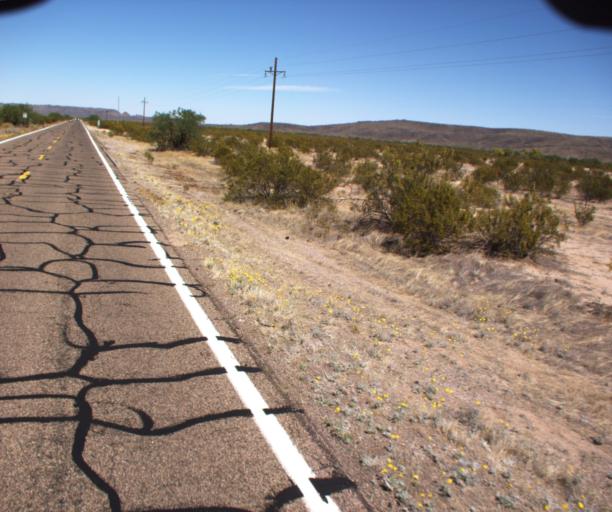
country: US
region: Arizona
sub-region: Pima County
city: Ajo
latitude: 32.4692
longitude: -112.8756
